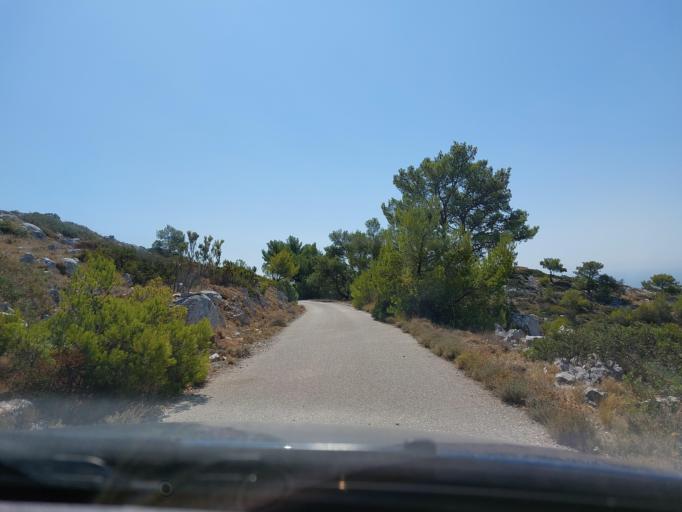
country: HR
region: Dubrovacko-Neretvanska
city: Smokvica
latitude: 42.7445
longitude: 16.8554
